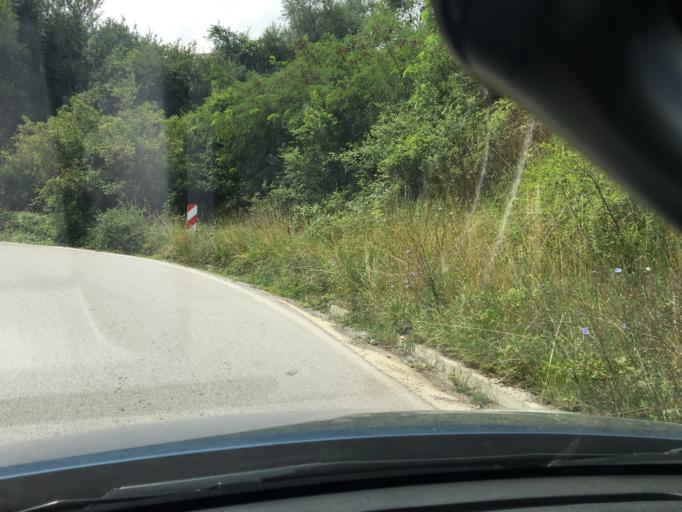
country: BG
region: Sofia-Capital
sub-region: Stolichna Obshtina
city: Sofia
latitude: 42.6002
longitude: 23.3679
